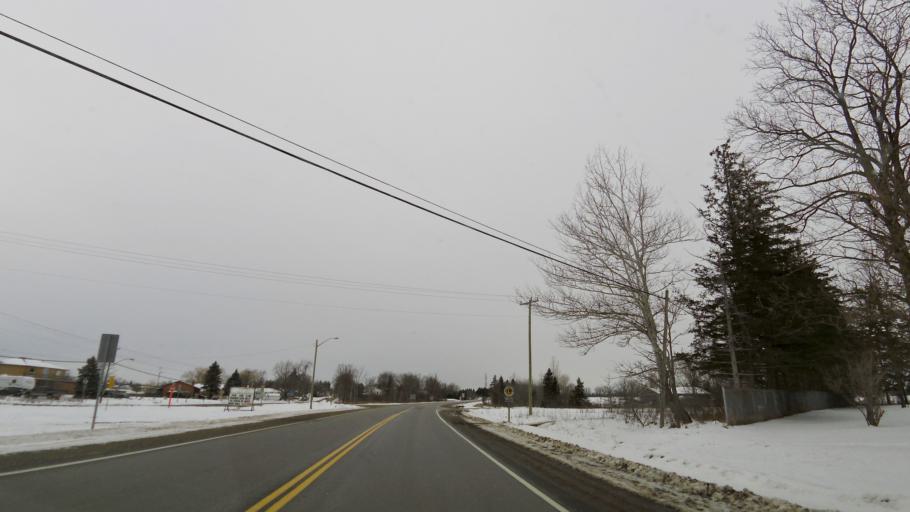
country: CA
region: Ontario
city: Cambridge
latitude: 43.3227
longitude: -80.1974
